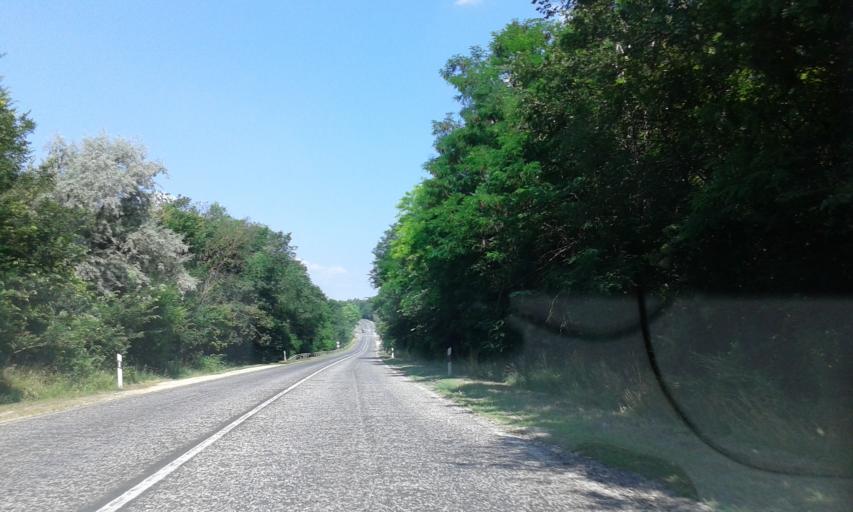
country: HU
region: Fejer
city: Etyek
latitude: 47.4882
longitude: 18.7676
